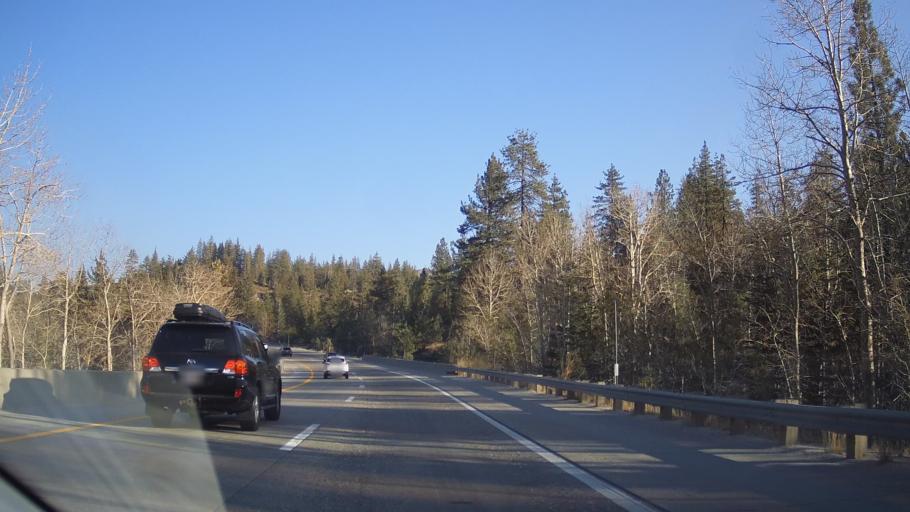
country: US
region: California
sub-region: Nevada County
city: Truckee
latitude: 39.3045
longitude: -120.5340
